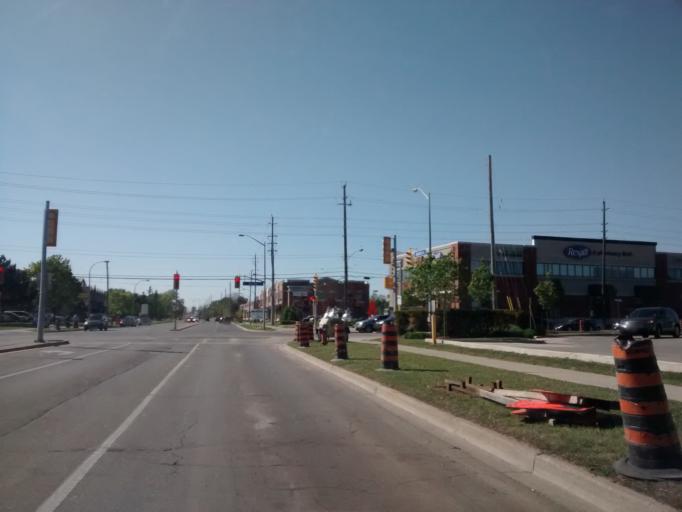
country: CA
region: Ontario
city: Burlington
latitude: 43.3669
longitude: -79.7532
